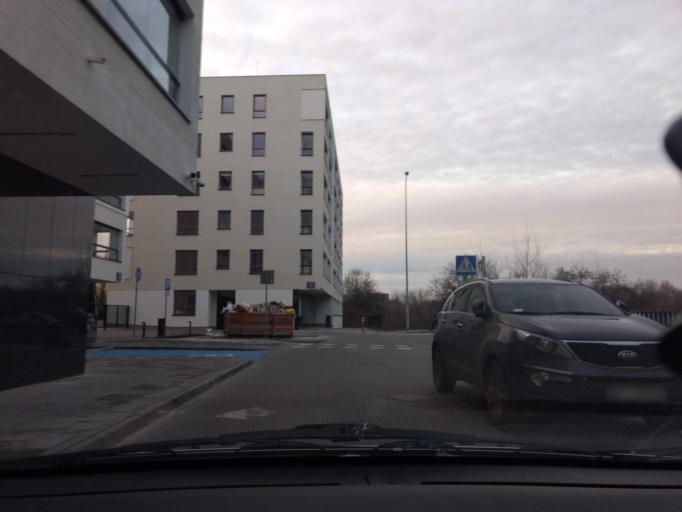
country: PL
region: Masovian Voivodeship
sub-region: Warszawa
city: Praga Poludnie
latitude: 52.2291
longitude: 21.0734
